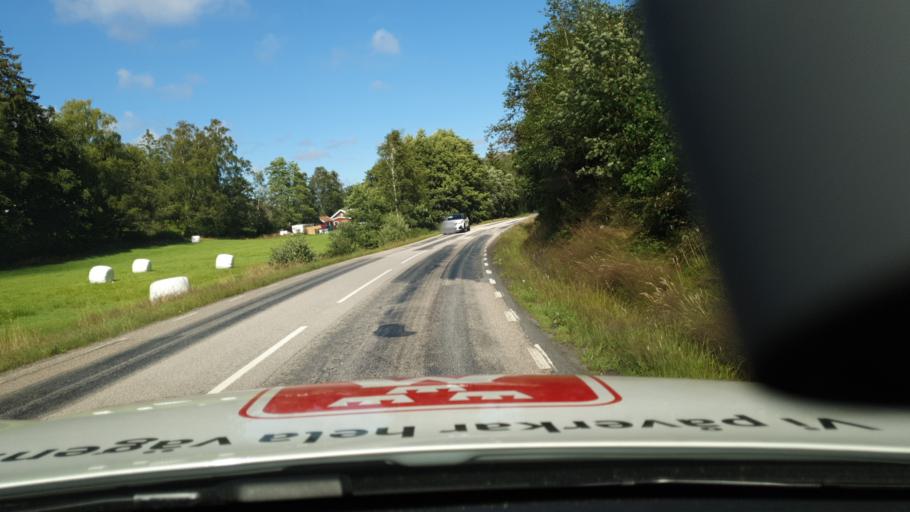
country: SE
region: Vaestra Goetaland
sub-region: Orust
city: Henan
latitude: 58.2208
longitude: 11.5999
